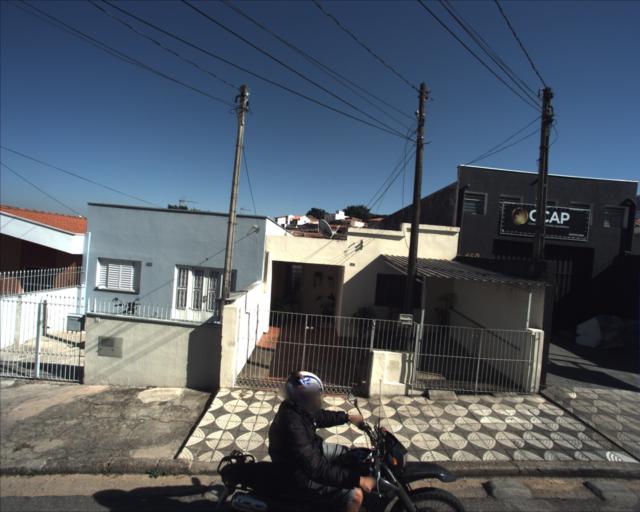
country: BR
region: Sao Paulo
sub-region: Sorocaba
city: Sorocaba
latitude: -23.5099
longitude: -47.4405
